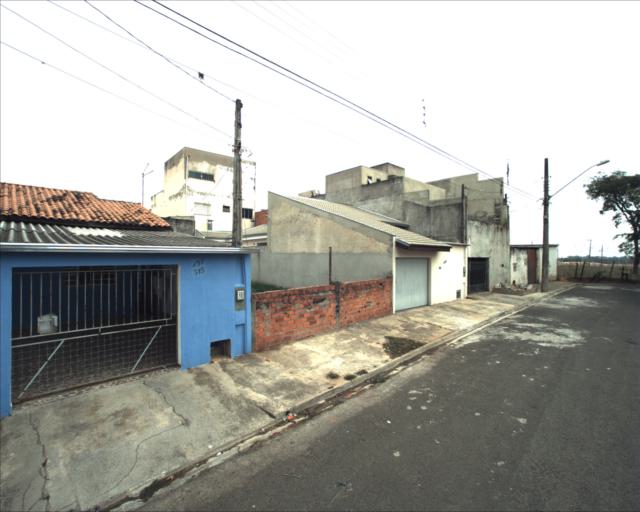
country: BR
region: Sao Paulo
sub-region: Sorocaba
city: Sorocaba
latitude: -23.4939
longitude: -47.5306
